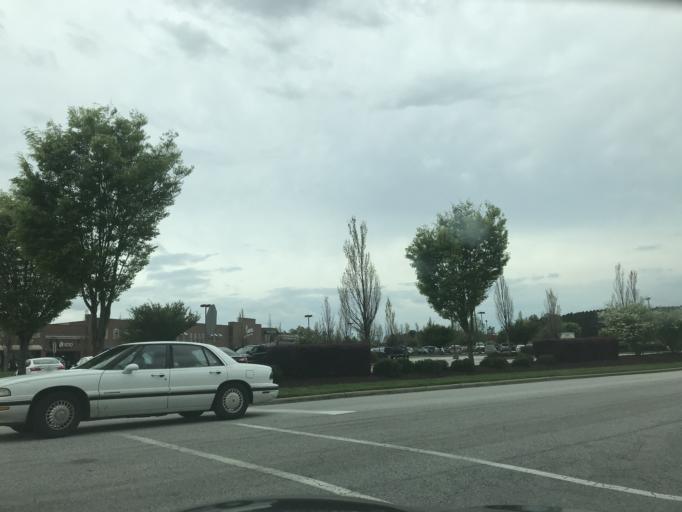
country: US
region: North Carolina
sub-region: Wake County
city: Wake Forest
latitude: 35.9685
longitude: -78.4951
